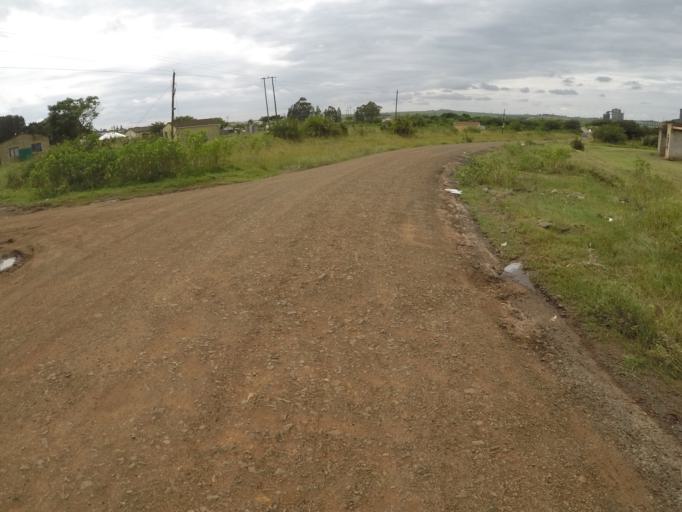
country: ZA
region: KwaZulu-Natal
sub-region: uThungulu District Municipality
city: Empangeni
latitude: -28.7129
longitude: 31.8627
